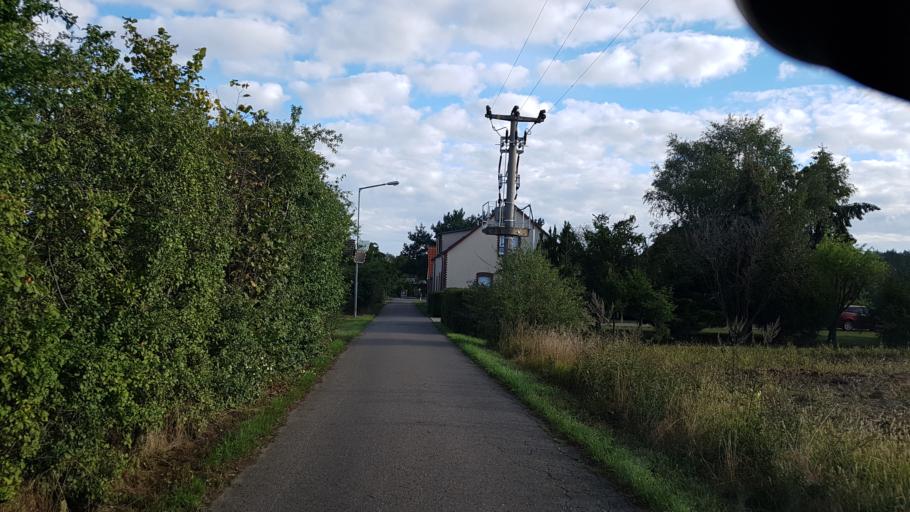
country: DE
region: Brandenburg
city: Welzow
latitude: 51.5552
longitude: 14.1760
